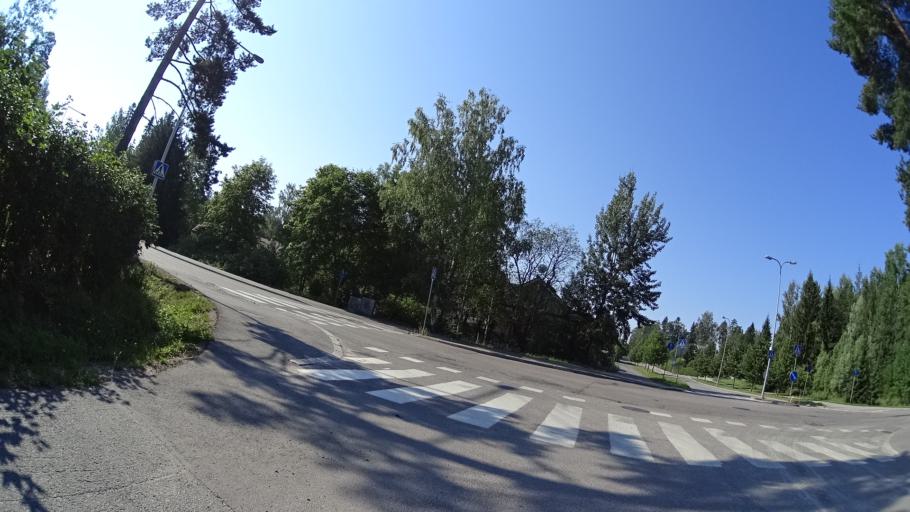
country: FI
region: Uusimaa
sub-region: Helsinki
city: Vantaa
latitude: 60.3290
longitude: 25.0881
